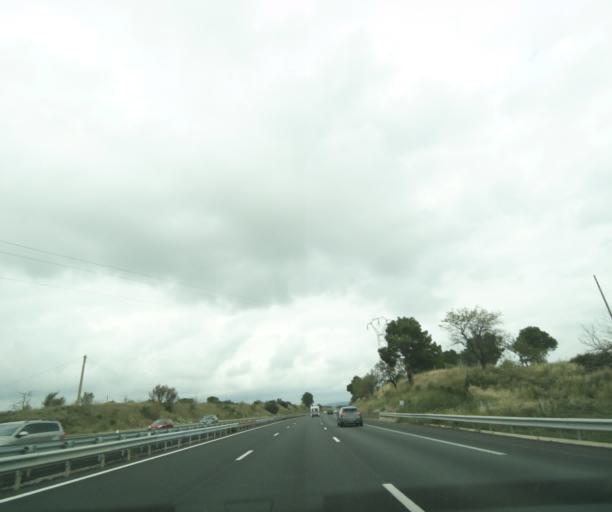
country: FR
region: Languedoc-Roussillon
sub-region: Departement de l'Herault
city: Meze
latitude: 43.4465
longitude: 3.5771
